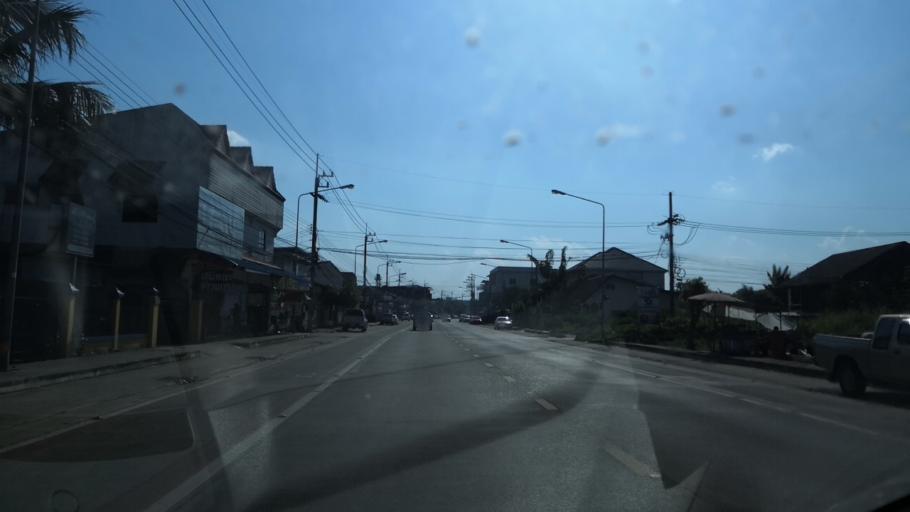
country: TH
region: Chiang Rai
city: Chiang Rai
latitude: 19.9301
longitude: 99.8393
